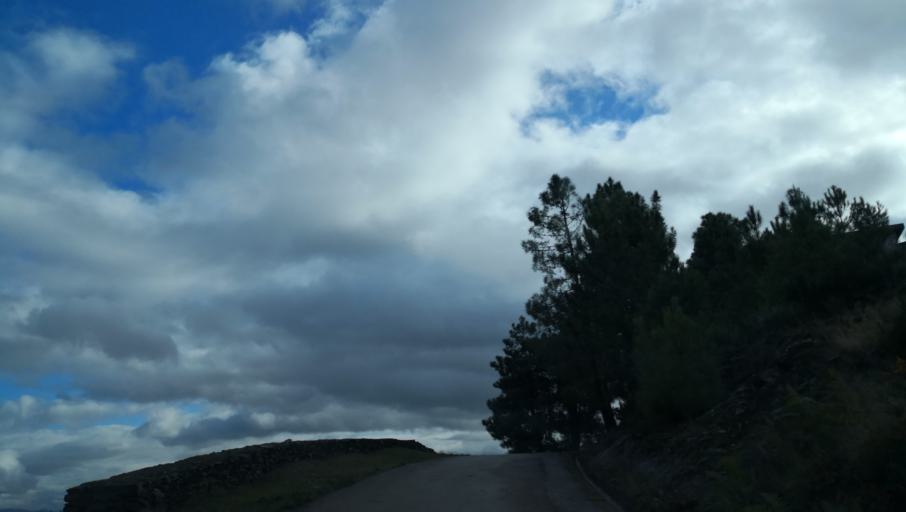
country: PT
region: Vila Real
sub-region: Sabrosa
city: Vilela
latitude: 41.1976
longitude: -7.5767
